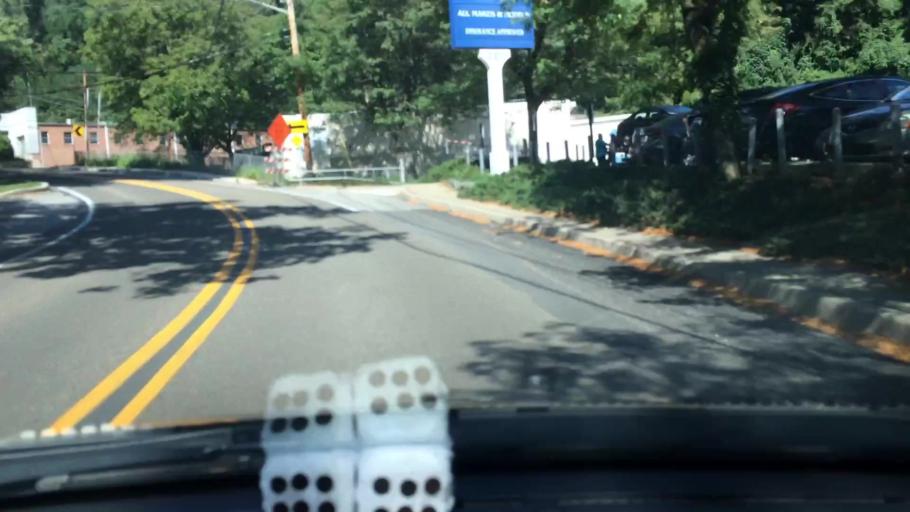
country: US
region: Pennsylvania
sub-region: Montgomery County
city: Bala-Cynwyd
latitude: 40.0219
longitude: -75.2338
